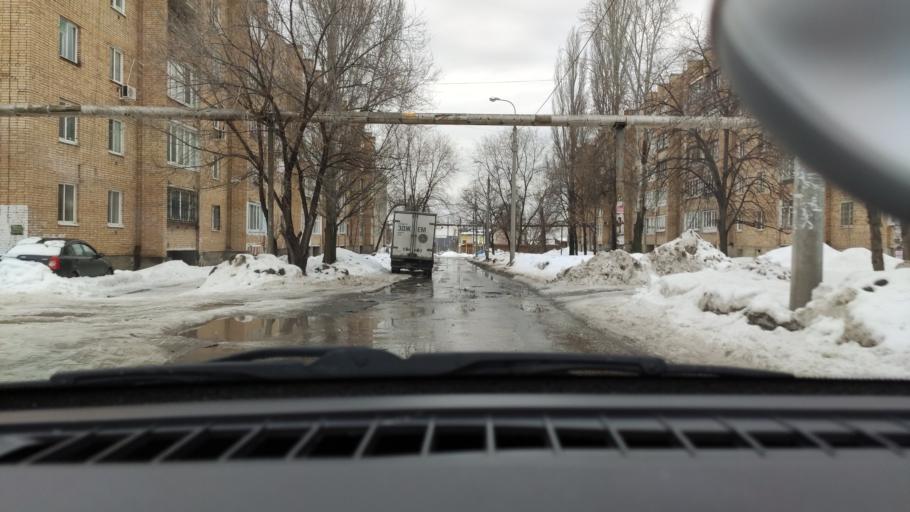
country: RU
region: Samara
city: Petra-Dubrava
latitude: 53.2979
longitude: 50.2813
